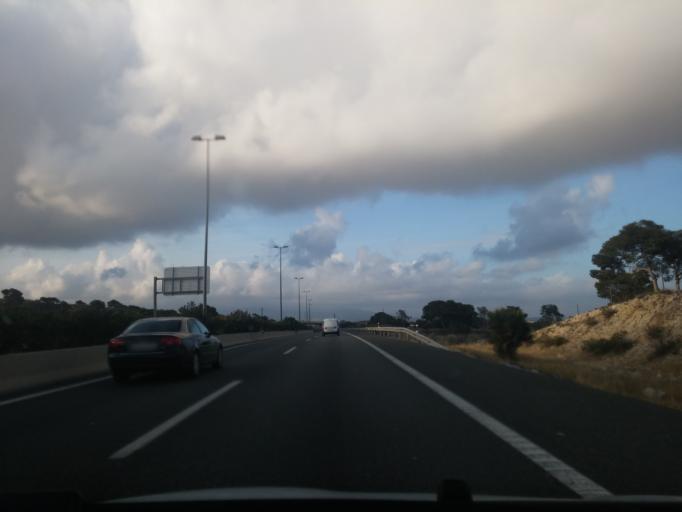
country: ES
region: Valencia
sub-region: Provincia de Alicante
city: San Juan de Alicante
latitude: 38.3889
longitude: -0.4534
